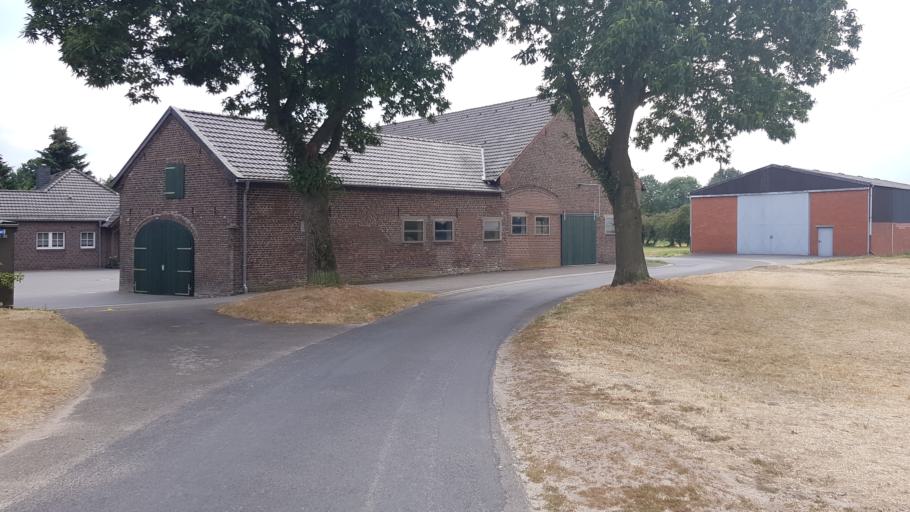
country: DE
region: North Rhine-Westphalia
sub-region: Regierungsbezirk Dusseldorf
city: Kamp-Lintfort
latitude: 51.4524
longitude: 6.5654
